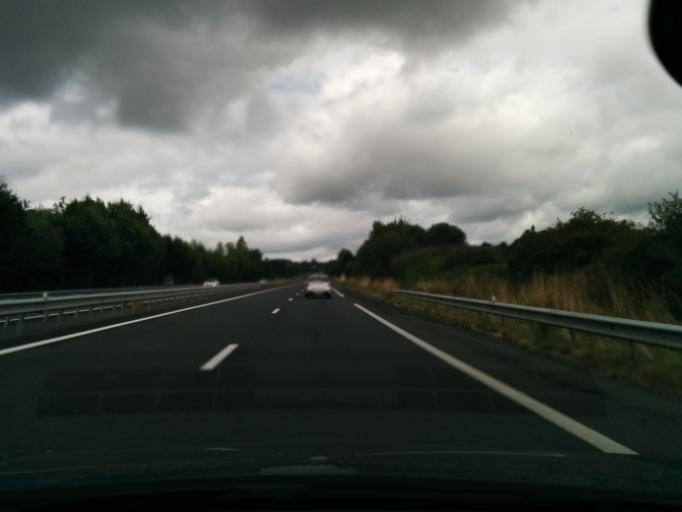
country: FR
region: Limousin
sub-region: Departement de la Correze
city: Vigeois
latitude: 45.4191
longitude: 1.5186
